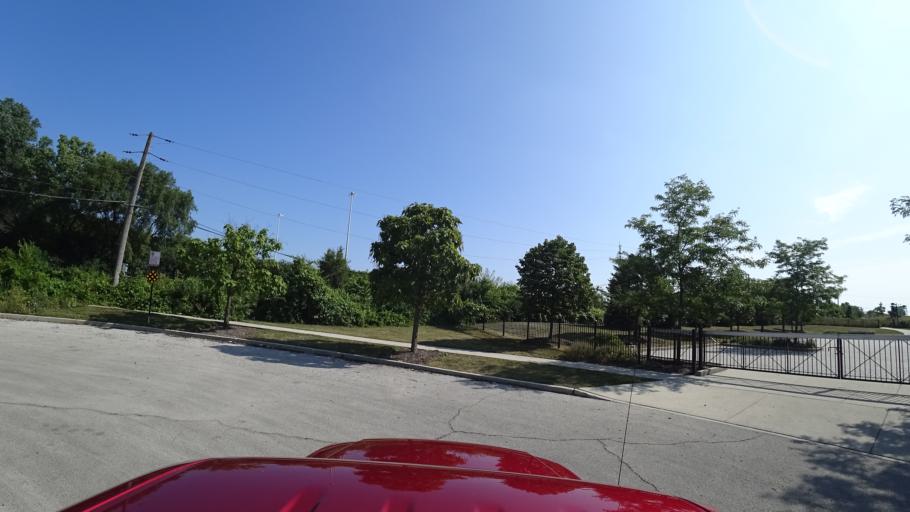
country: US
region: Illinois
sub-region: Cook County
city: Cicero
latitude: 41.8257
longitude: -87.7116
